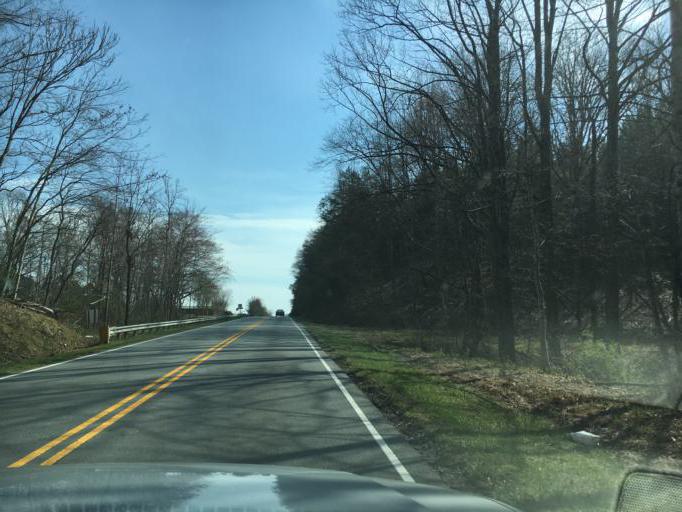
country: US
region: North Carolina
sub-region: McDowell County
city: West Marion
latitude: 35.6041
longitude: -81.9846
